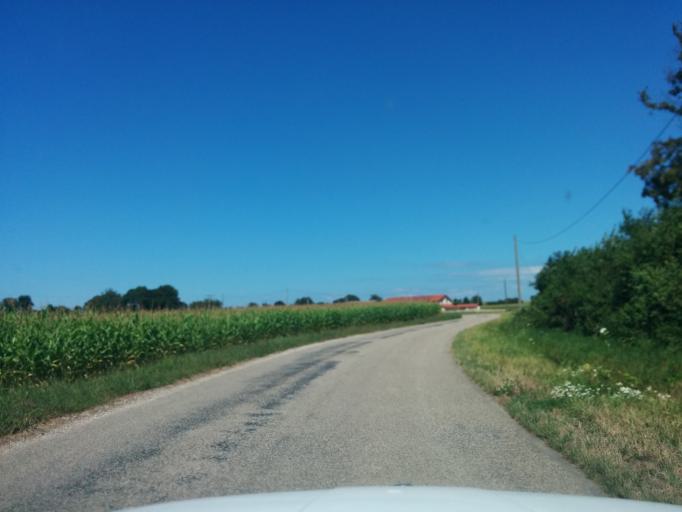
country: FR
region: Rhone-Alpes
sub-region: Departement de l'Ain
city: Perouges
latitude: 45.9216
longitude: 5.1501
